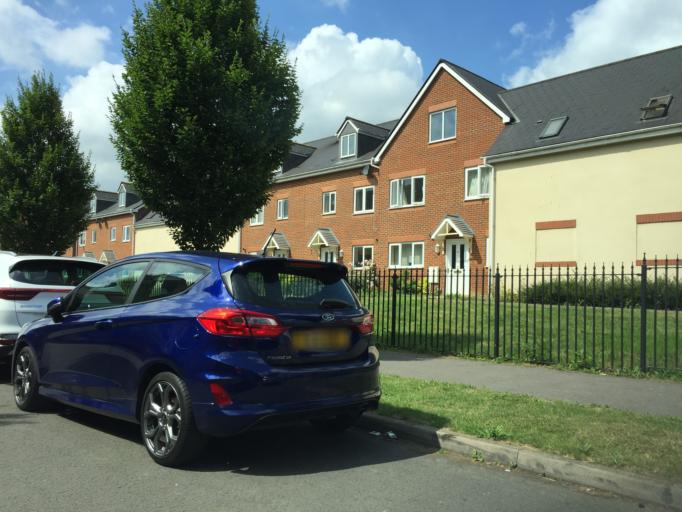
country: GB
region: England
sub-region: Gloucestershire
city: Gloucester
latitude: 51.8743
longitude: -2.2517
